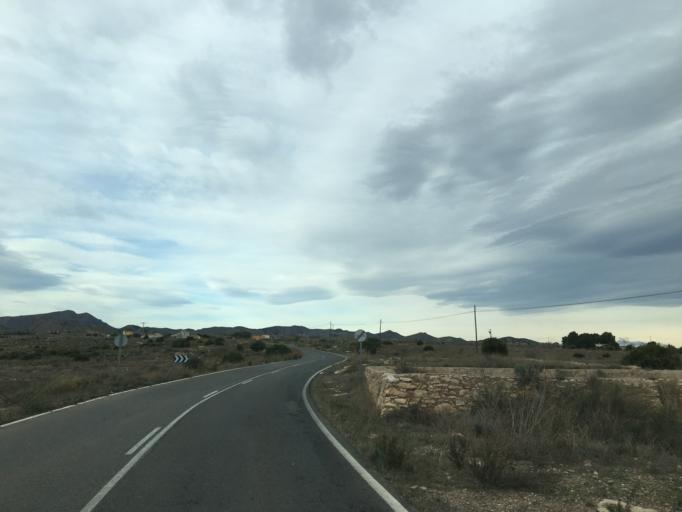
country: ES
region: Murcia
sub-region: Murcia
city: Fuente-Alamo de Murcia
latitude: 37.6193
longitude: -1.0768
